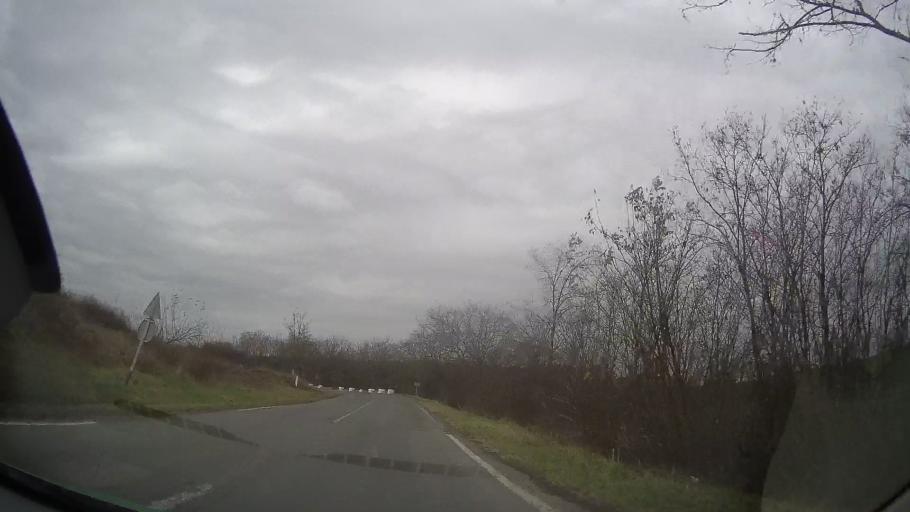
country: RO
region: Mures
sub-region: Comuna Faragau
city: Faragau
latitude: 46.7637
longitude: 24.5297
